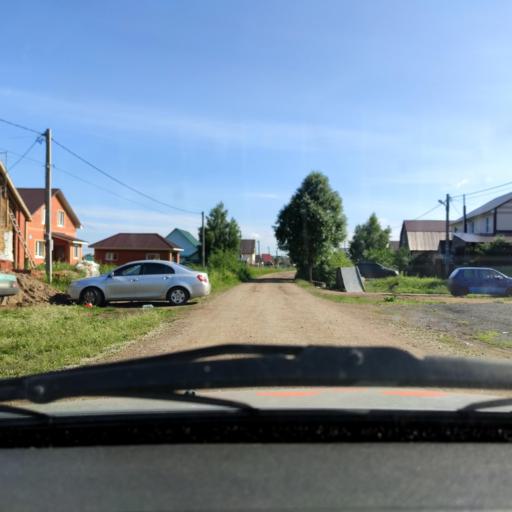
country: RU
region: Bashkortostan
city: Iglino
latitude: 54.7982
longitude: 56.2981
